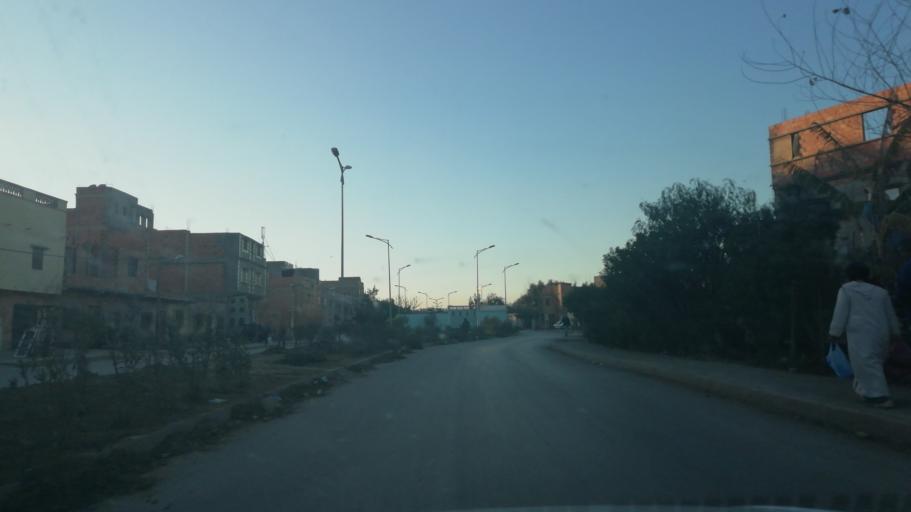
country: DZ
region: Oran
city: Es Senia
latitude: 35.6501
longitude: -0.5768
